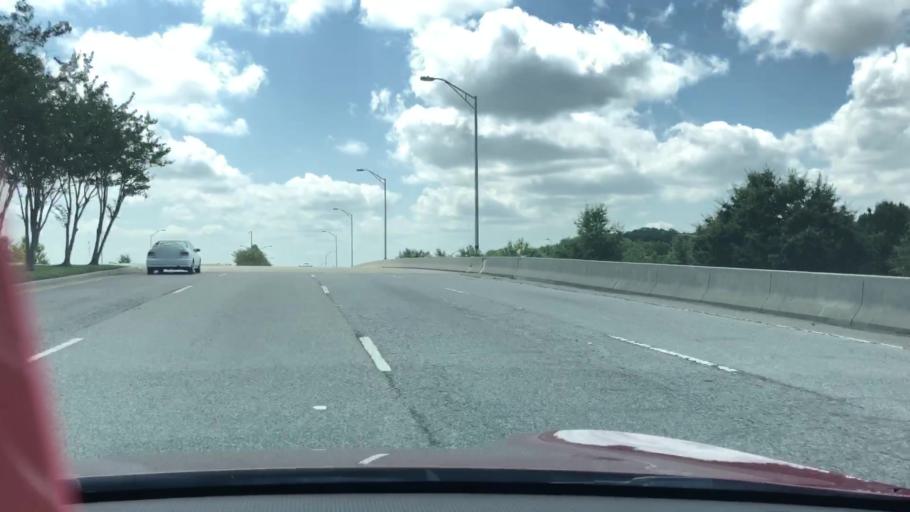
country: US
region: Virginia
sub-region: City of Chesapeake
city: Chesapeake
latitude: 36.8567
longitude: -76.2100
